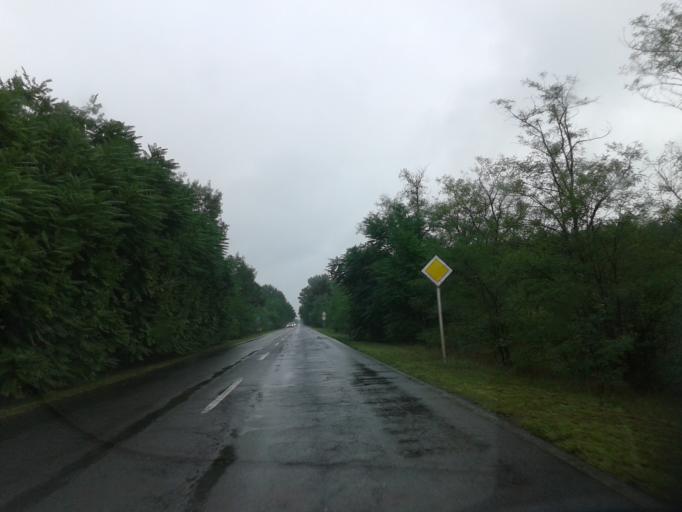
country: HU
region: Csongrad
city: Asotthalom
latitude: 46.2228
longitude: 19.7678
